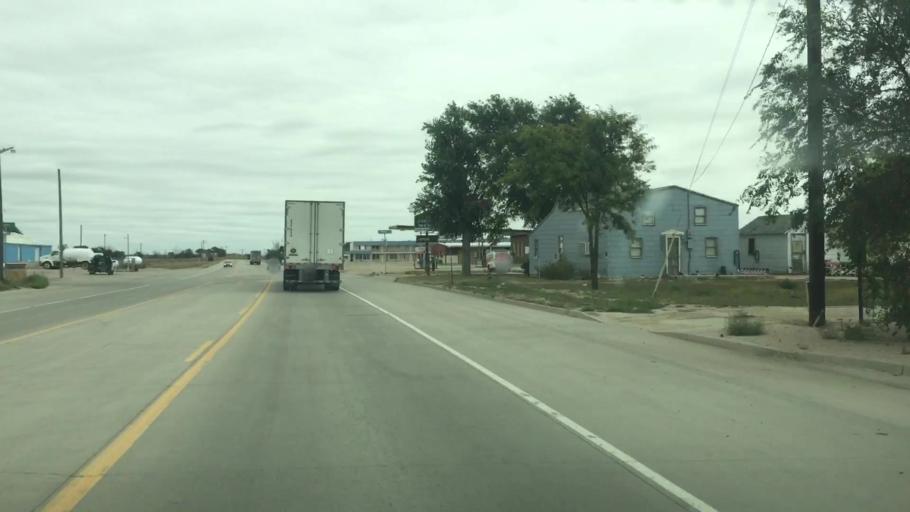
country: US
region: Colorado
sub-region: Kiowa County
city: Eads
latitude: 38.4774
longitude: -102.7772
